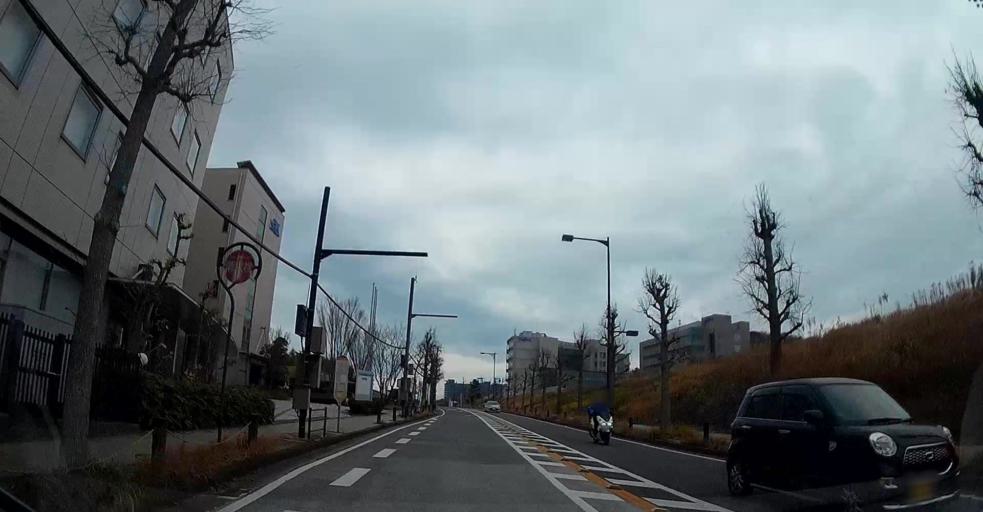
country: JP
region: Kanagawa
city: Yokosuka
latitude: 35.2226
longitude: 139.6770
